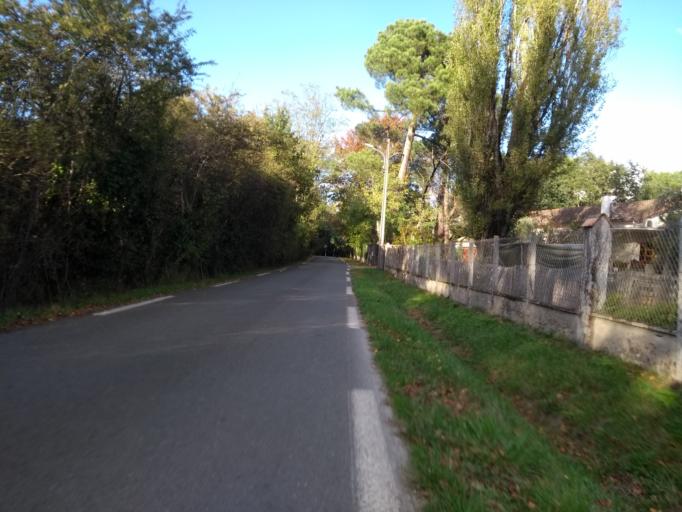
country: FR
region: Aquitaine
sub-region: Departement de la Gironde
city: Gradignan
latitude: 44.7562
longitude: -0.6176
